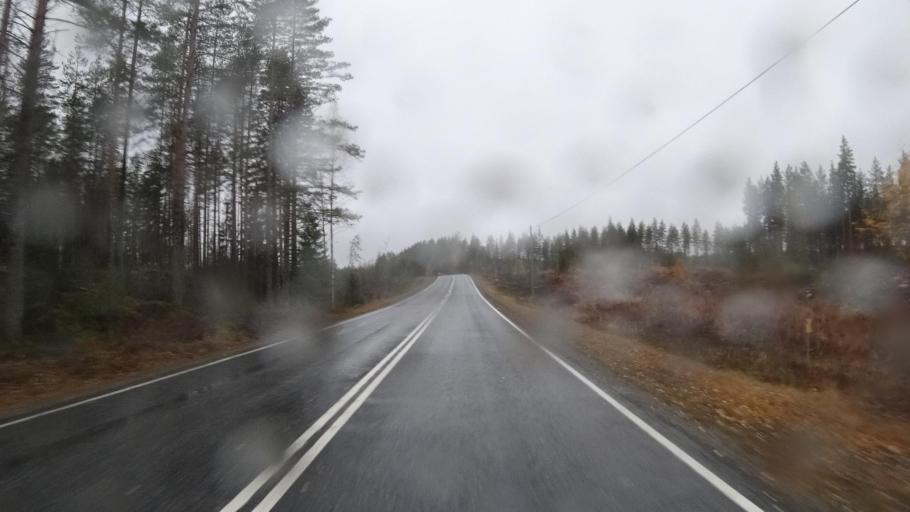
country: FI
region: Northern Savo
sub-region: Koillis-Savo
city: Tuusniemi
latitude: 62.8681
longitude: 28.4176
